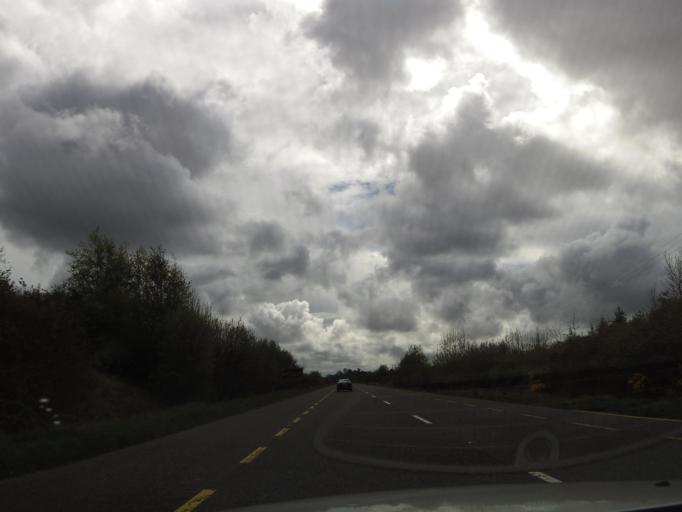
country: IE
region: Connaught
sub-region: Maigh Eo
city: Claremorris
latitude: 53.7330
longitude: -8.9758
